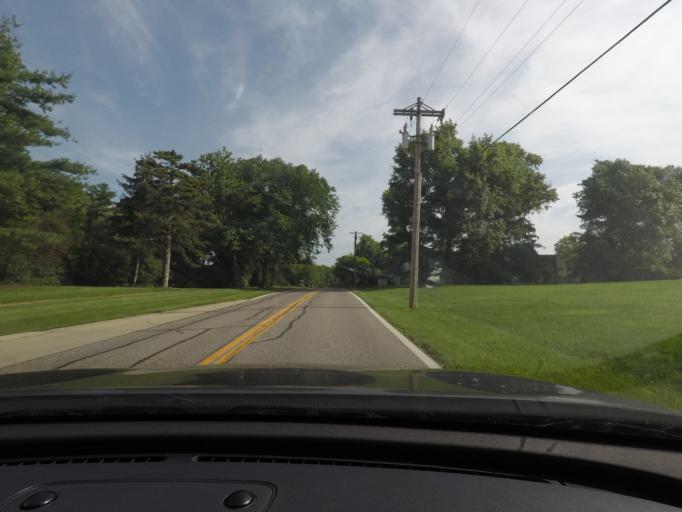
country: US
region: Missouri
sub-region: Saint Louis County
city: Town and Country
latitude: 38.6257
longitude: -90.4831
